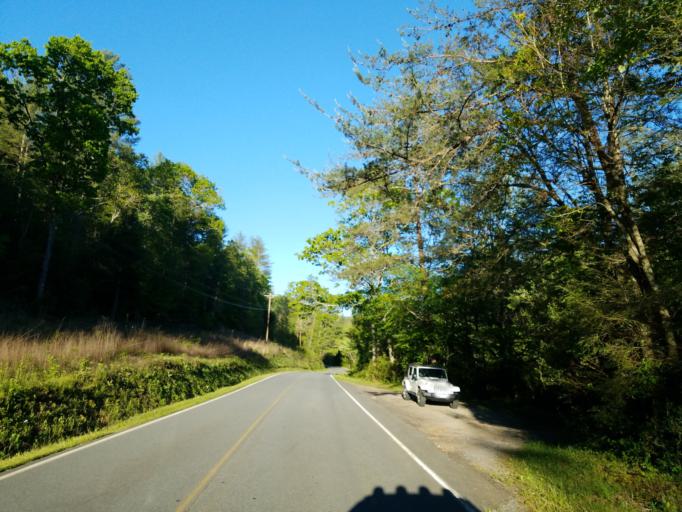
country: US
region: Georgia
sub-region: Fannin County
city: Blue Ridge
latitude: 34.7580
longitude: -84.2012
